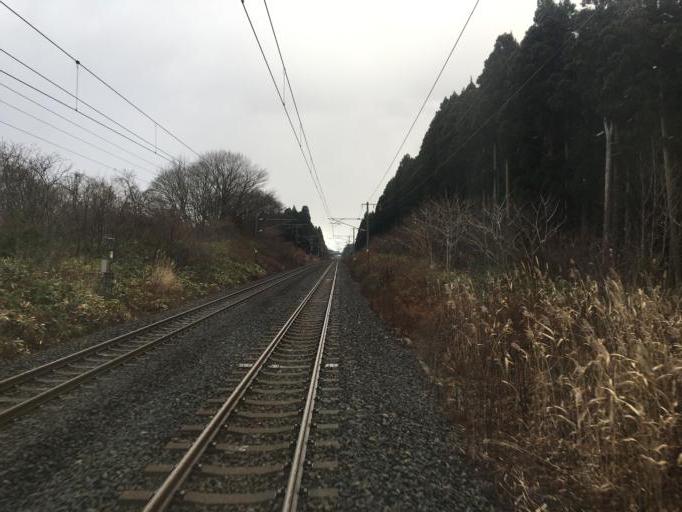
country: JP
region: Aomori
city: Aomori Shi
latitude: 40.9306
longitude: 140.9708
